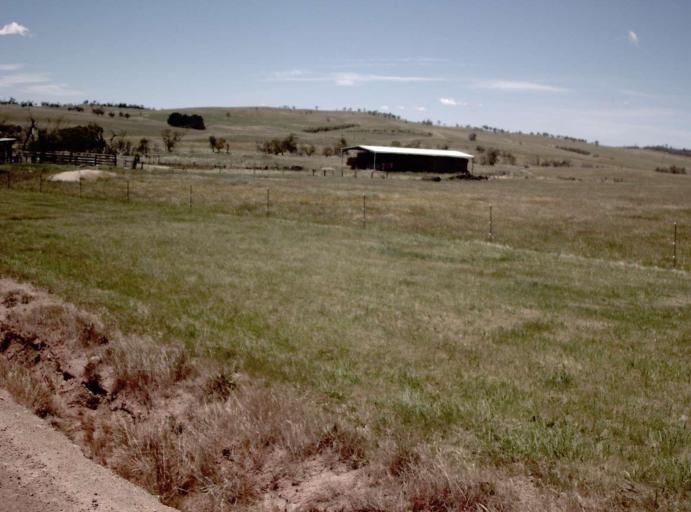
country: AU
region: New South Wales
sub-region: Snowy River
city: Jindabyne
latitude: -37.0141
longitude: 148.2778
